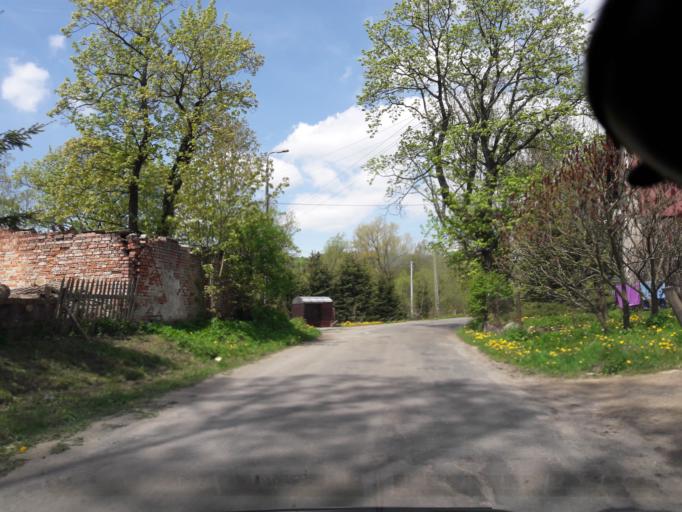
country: PL
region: Lower Silesian Voivodeship
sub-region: Powiat klodzki
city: Duszniki-Zdroj
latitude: 50.4283
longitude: 16.3618
